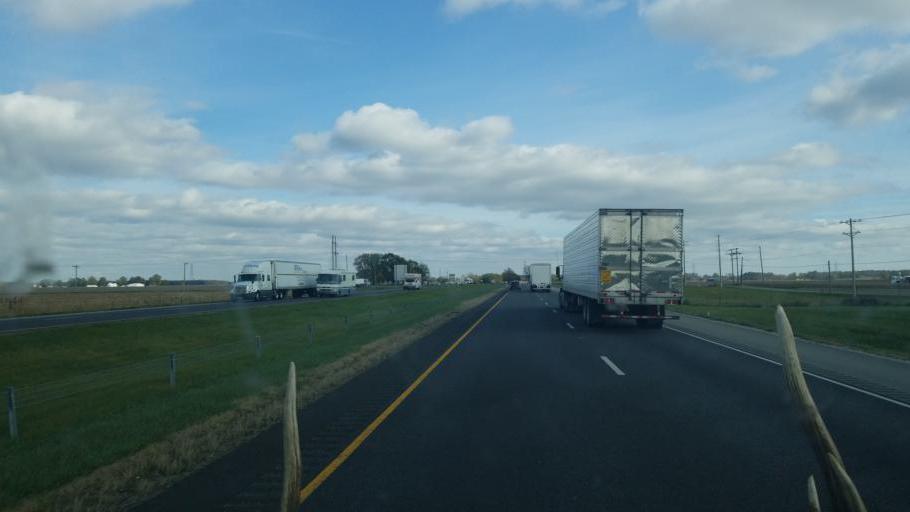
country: US
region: Indiana
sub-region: Wayne County
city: Cambridge City
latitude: 39.8526
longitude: -85.1277
